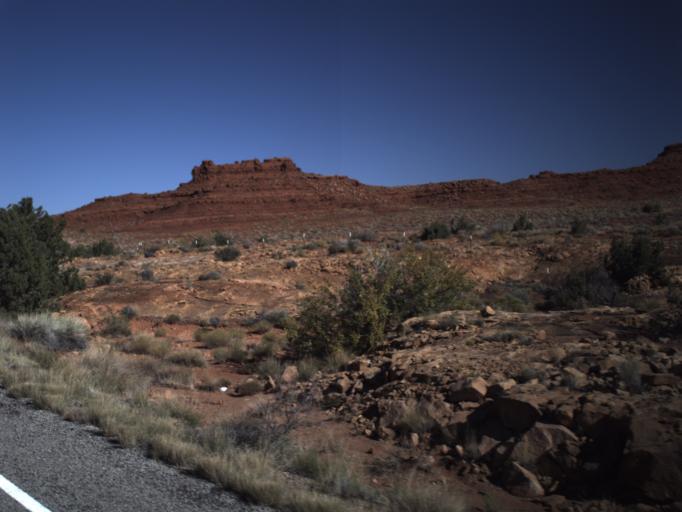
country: US
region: Utah
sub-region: San Juan County
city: Blanding
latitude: 37.8226
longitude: -110.3569
